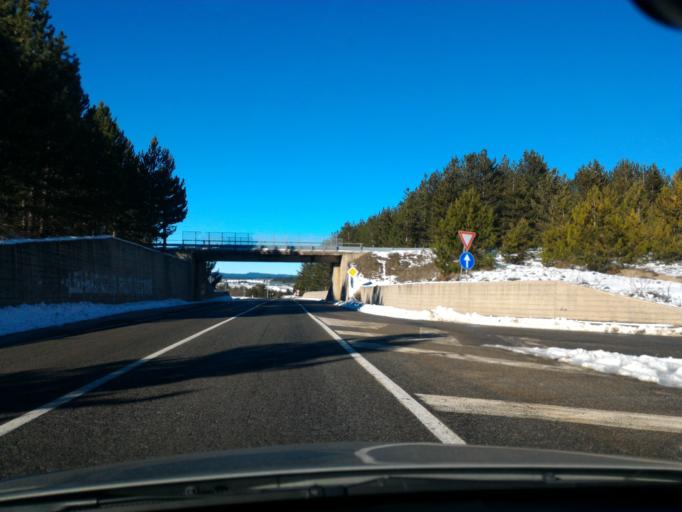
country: IT
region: Calabria
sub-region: Provincia di Cosenza
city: Longobucco
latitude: 39.3162
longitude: 16.5471
